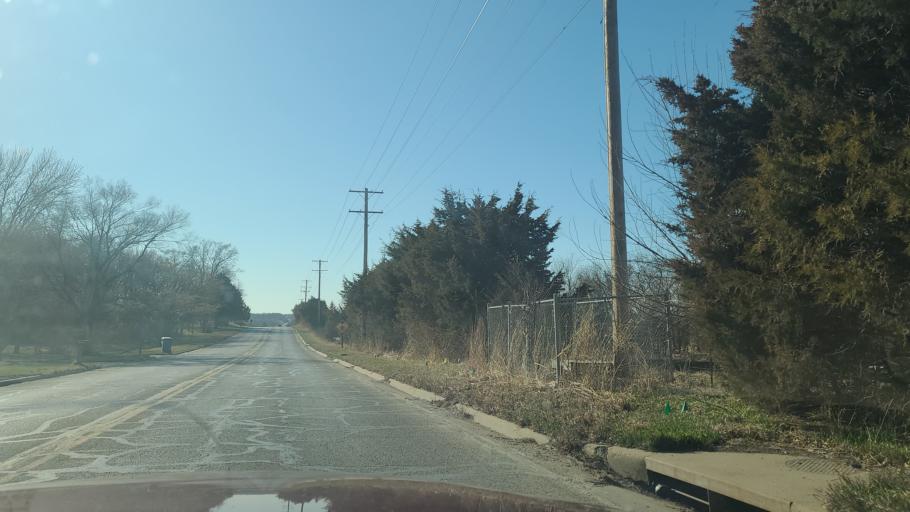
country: US
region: Kansas
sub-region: Douglas County
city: Lawrence
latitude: 39.0007
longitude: -95.2756
